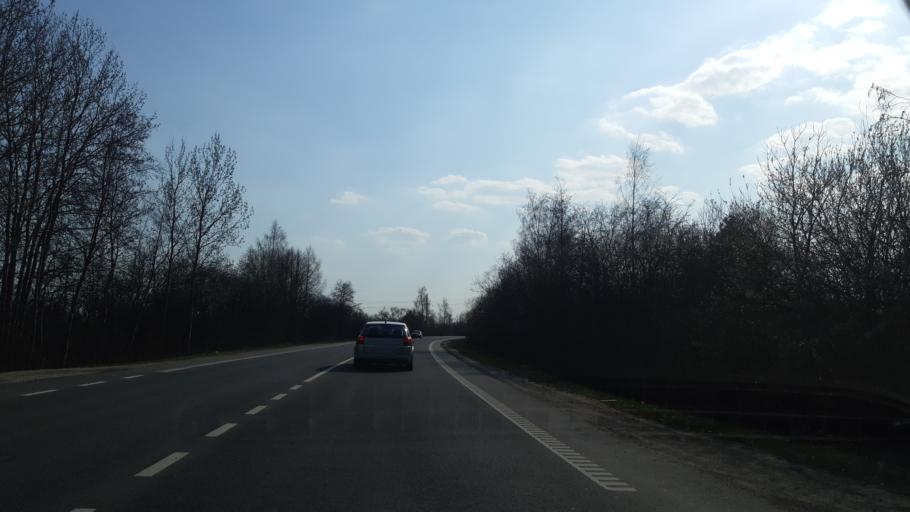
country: LT
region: Kauno apskritis
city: Dainava (Kaunas)
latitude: 54.8619
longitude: 23.9853
